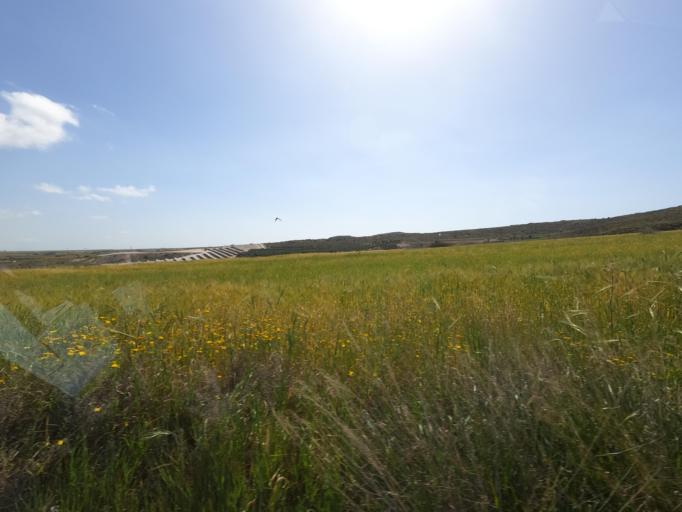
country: CY
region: Lefkosia
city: Astromeritis
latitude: 35.0902
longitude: 33.0216
